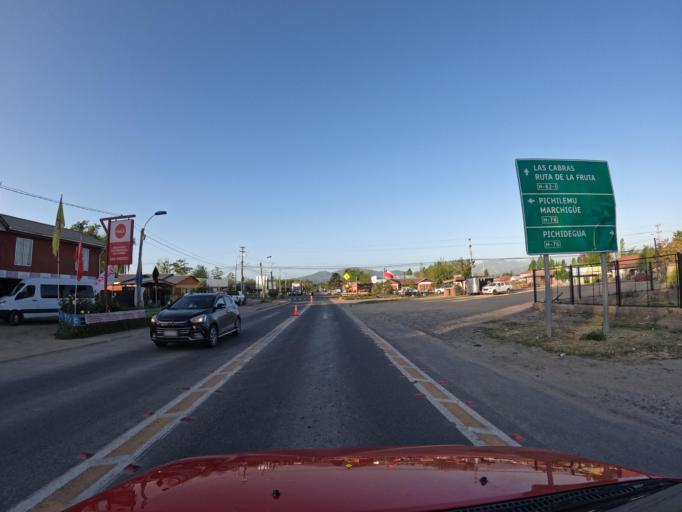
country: CL
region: O'Higgins
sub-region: Provincia de Cachapoal
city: San Vicente
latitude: -34.3122
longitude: -71.3843
